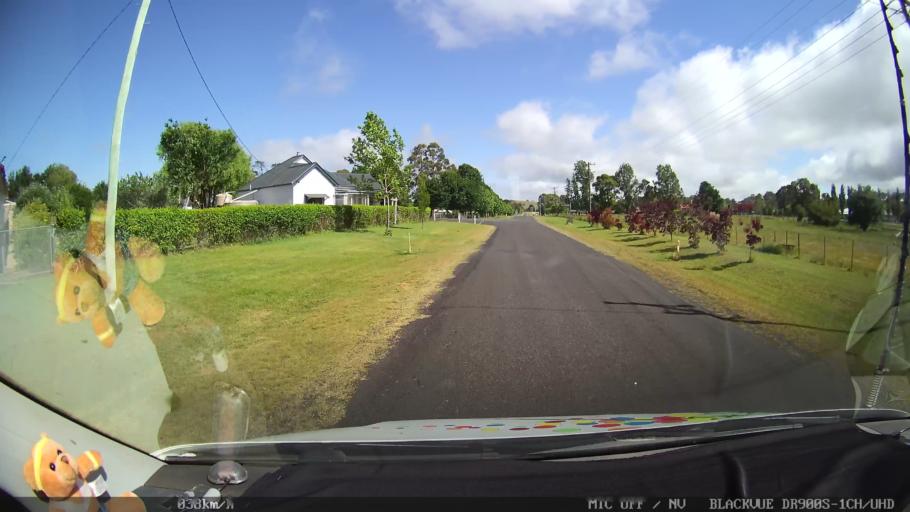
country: AU
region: New South Wales
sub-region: Guyra
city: Guyra
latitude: -30.0233
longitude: 151.6600
